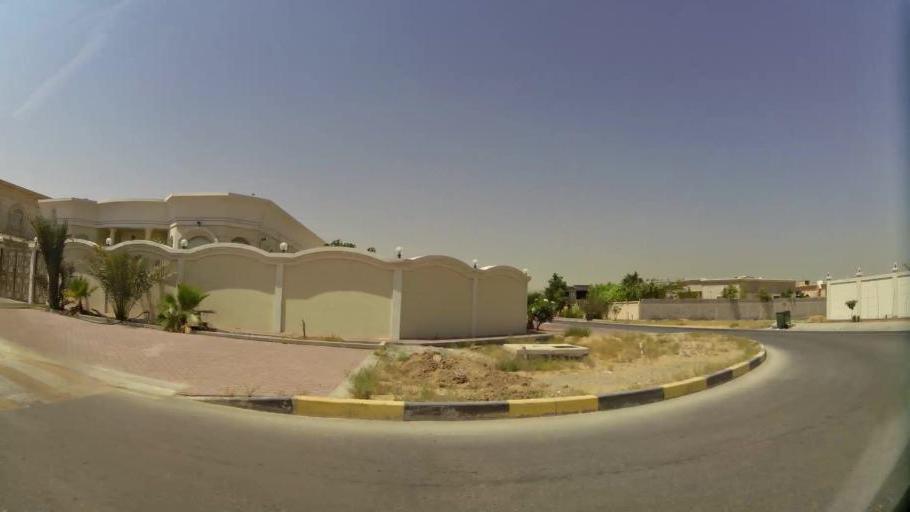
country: AE
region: Ajman
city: Ajman
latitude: 25.4172
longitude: 55.5175
